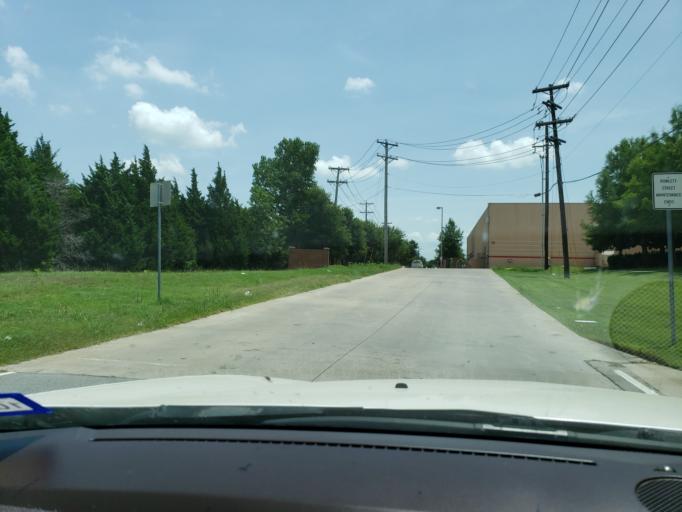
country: US
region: Texas
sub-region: Dallas County
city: Rowlett
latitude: 32.9096
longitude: -96.5600
